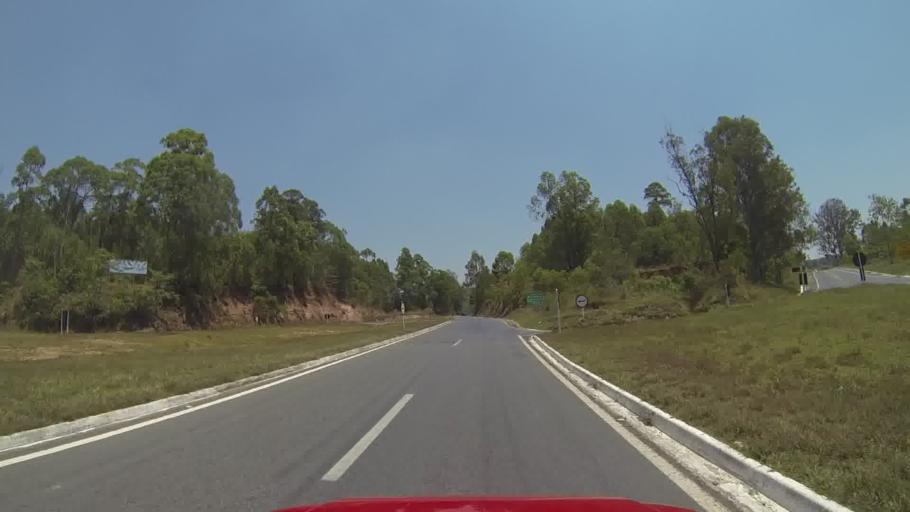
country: BR
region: Minas Gerais
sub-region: Itapecerica
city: Itapecerica
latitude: -20.2970
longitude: -45.1818
